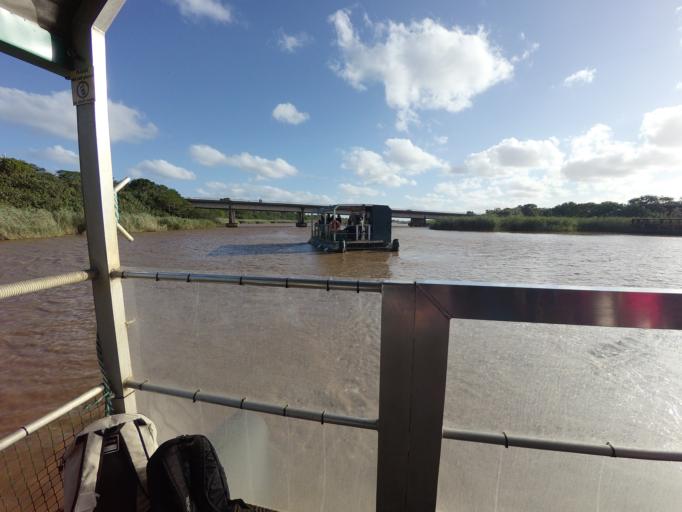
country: ZA
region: KwaZulu-Natal
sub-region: uMkhanyakude District Municipality
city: Mtubatuba
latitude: -28.3691
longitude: 32.4104
